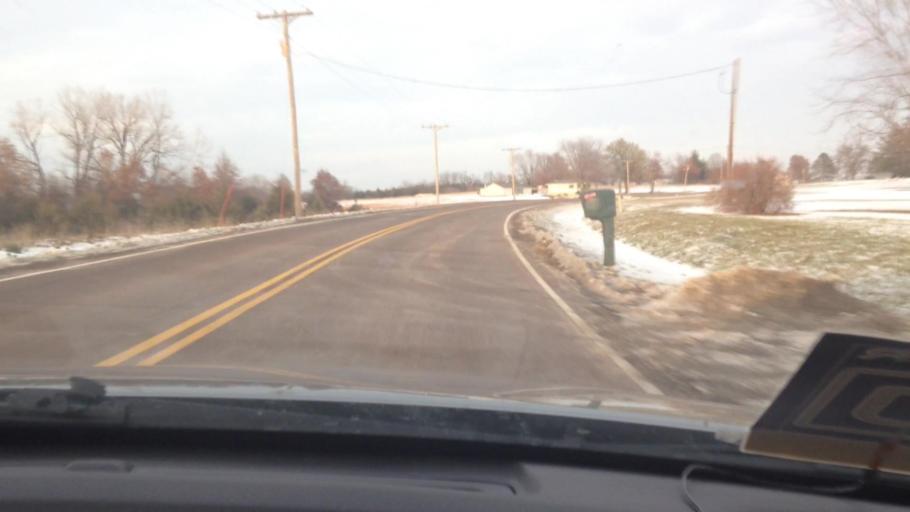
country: US
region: Kansas
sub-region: Leavenworth County
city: Lansing
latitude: 39.2335
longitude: -94.9838
